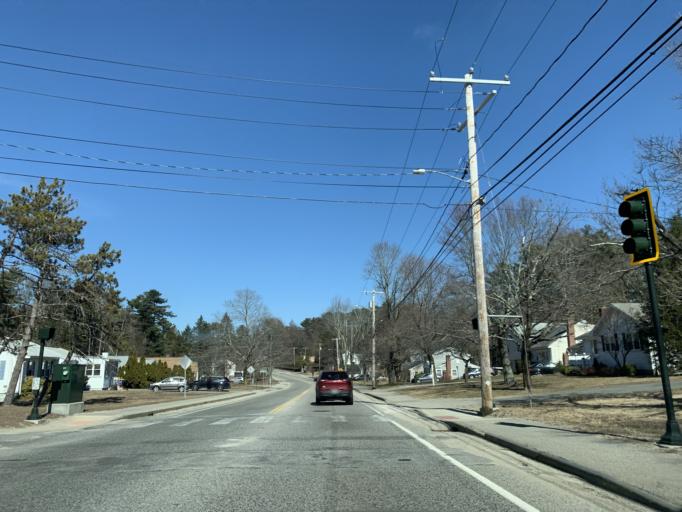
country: US
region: Massachusetts
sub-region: Norfolk County
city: Sharon
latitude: 42.1140
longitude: -71.1864
